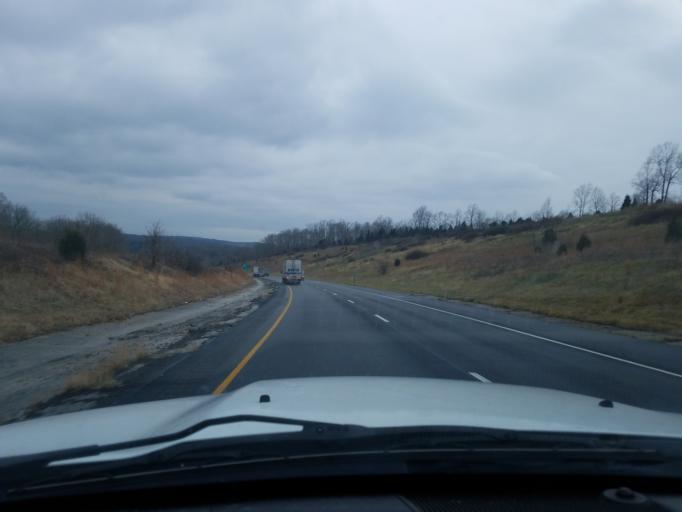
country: US
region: Indiana
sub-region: Crawford County
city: English
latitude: 38.2448
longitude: -86.4472
